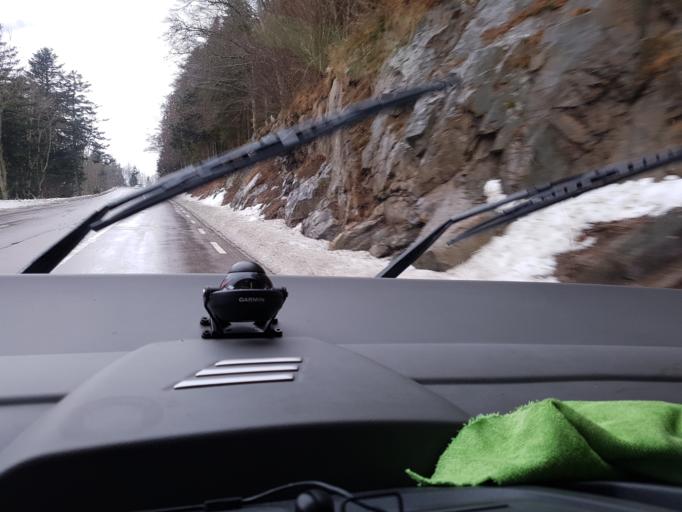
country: FR
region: Lorraine
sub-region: Departement des Vosges
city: Plainfaing
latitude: 48.1669
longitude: 7.0651
